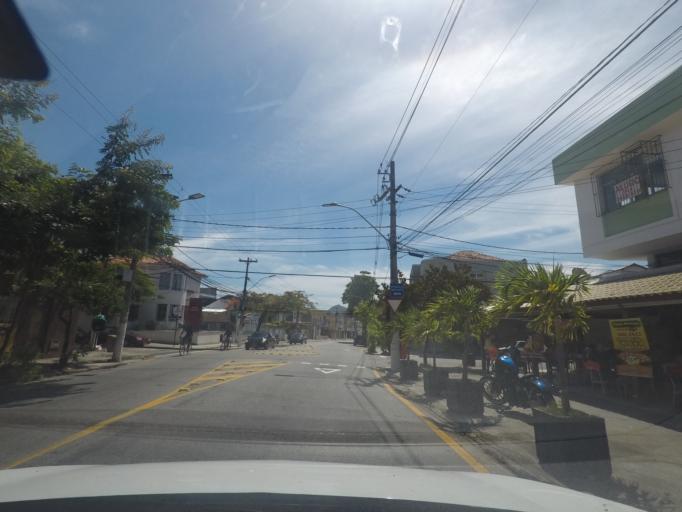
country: BR
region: Rio de Janeiro
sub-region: Niteroi
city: Niteroi
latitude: -22.9197
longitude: -43.0883
